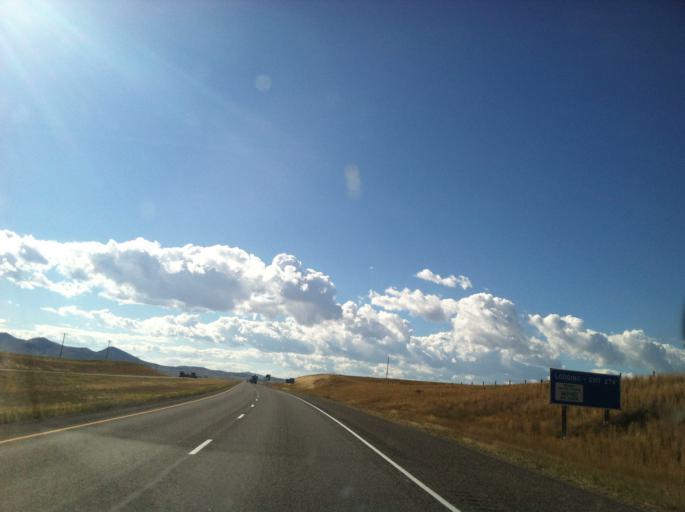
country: US
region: Montana
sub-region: Gallatin County
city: Three Forks
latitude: 45.9187
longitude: -111.5637
